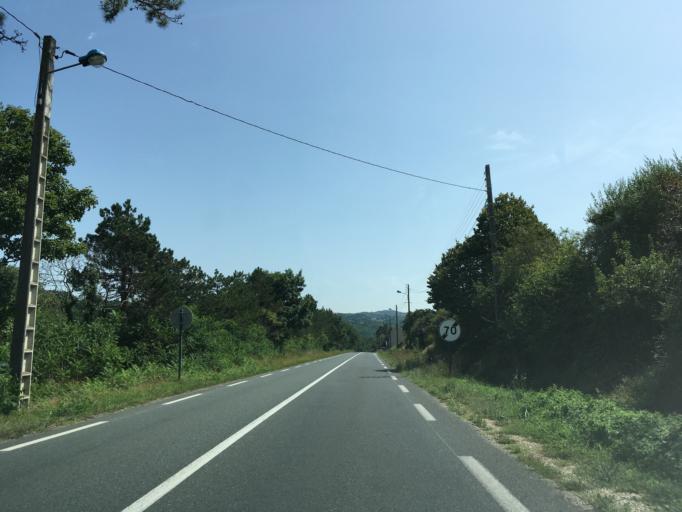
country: FR
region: Midi-Pyrenees
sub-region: Departement du Tarn
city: Castres
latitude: 43.6211
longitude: 2.2821
